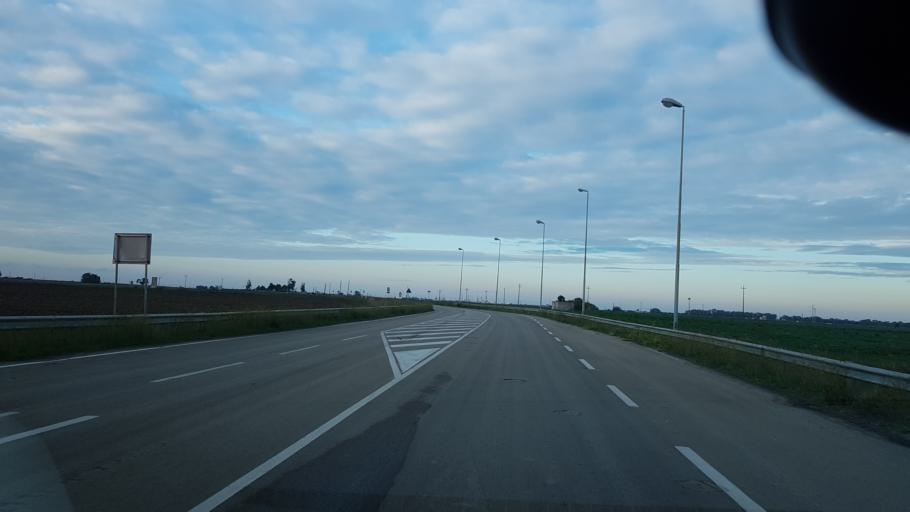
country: IT
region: Apulia
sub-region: Provincia di Brindisi
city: Tuturano
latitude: 40.5696
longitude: 18.0158
